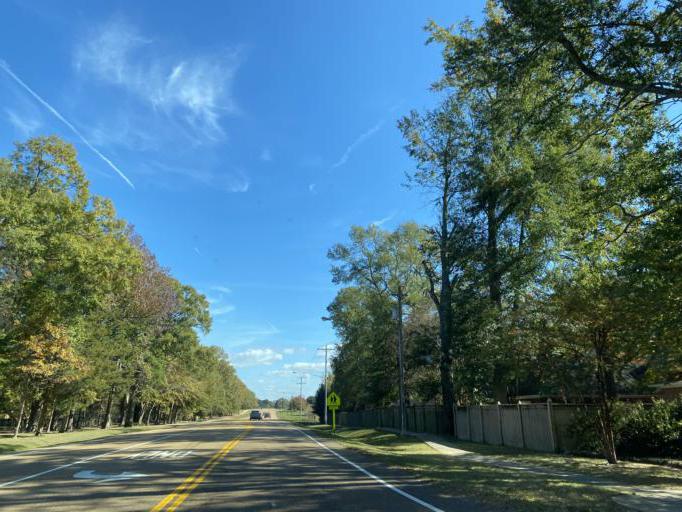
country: US
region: Mississippi
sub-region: Madison County
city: Madison
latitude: 32.4575
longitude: -90.0990
